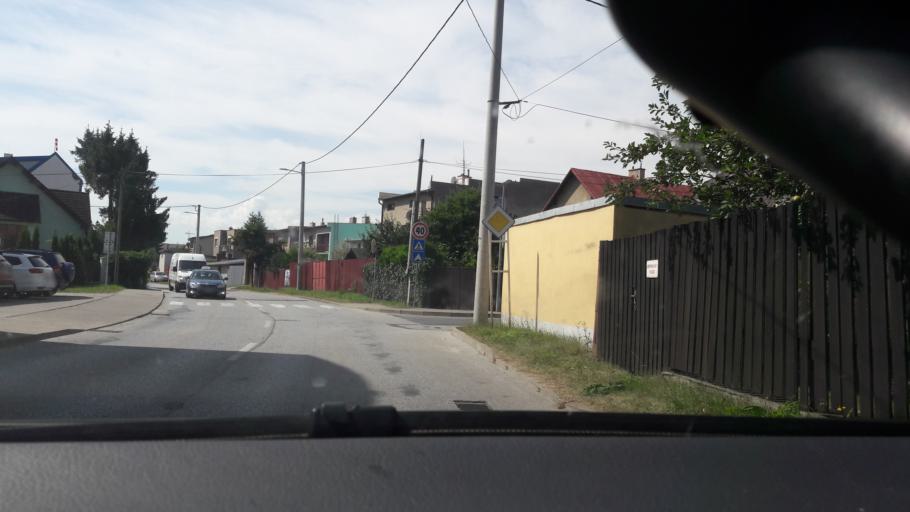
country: SK
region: Presovsky
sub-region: Okres Presov
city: Kezmarok
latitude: 49.1372
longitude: 20.4335
